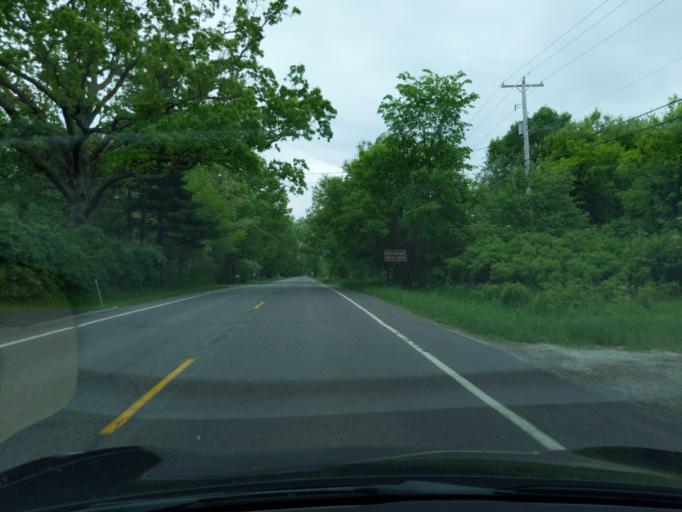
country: US
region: Michigan
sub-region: Ingham County
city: Haslett
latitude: 42.7341
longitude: -84.3635
